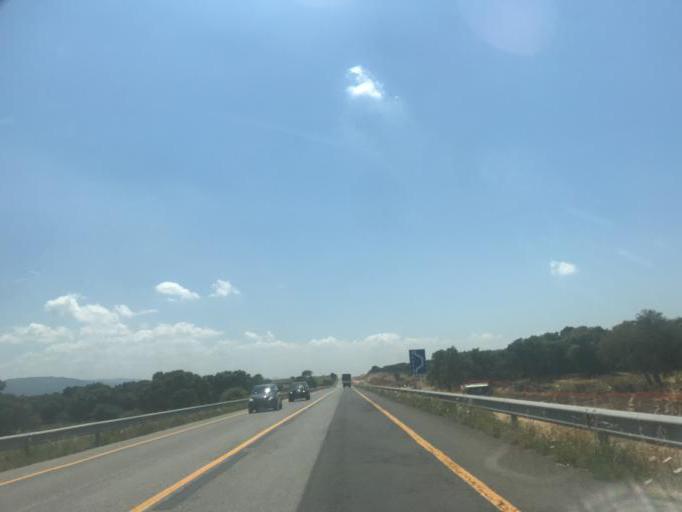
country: IT
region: Sardinia
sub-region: Provincia di Olbia-Tempio
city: Monti
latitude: 40.7915
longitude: 9.2632
